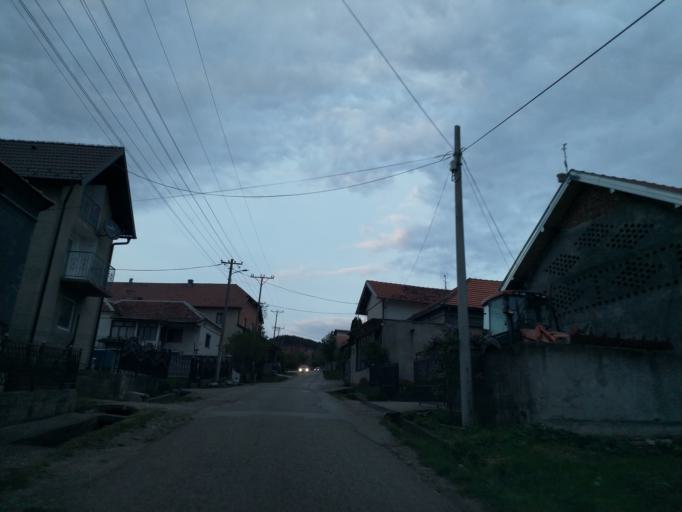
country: RS
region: Central Serbia
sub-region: Pomoravski Okrug
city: Paracin
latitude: 43.9406
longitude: 21.4975
